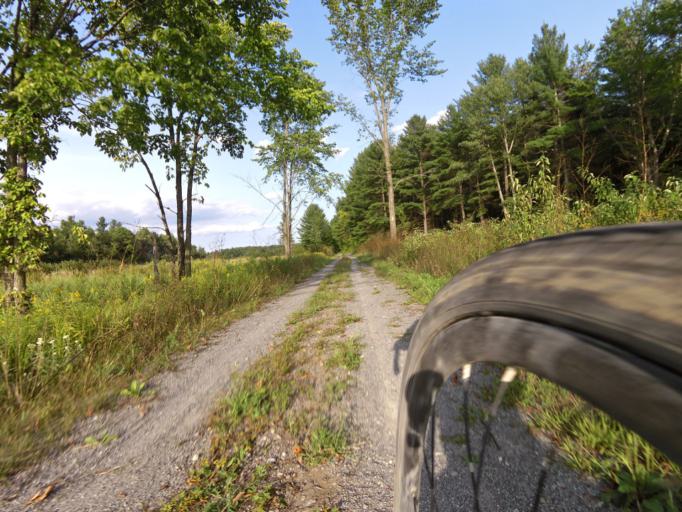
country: CA
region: Ontario
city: Kingston
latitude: 44.4860
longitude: -76.4614
